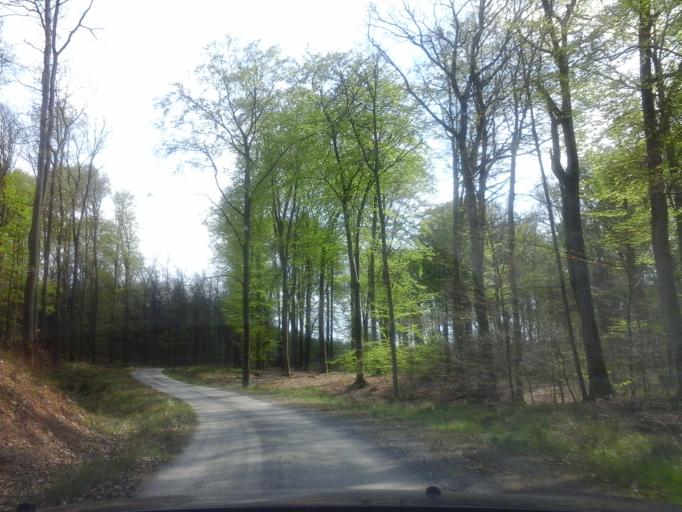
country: PL
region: West Pomeranian Voivodeship
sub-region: Powiat choszczenski
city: Krzecin
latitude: 53.0057
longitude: 15.4795
